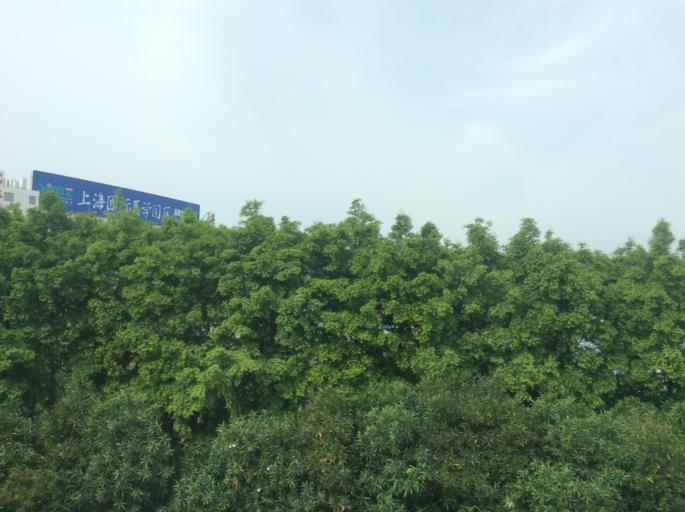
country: CN
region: Shanghai Shi
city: Laogang
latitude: 31.1822
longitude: 121.7834
